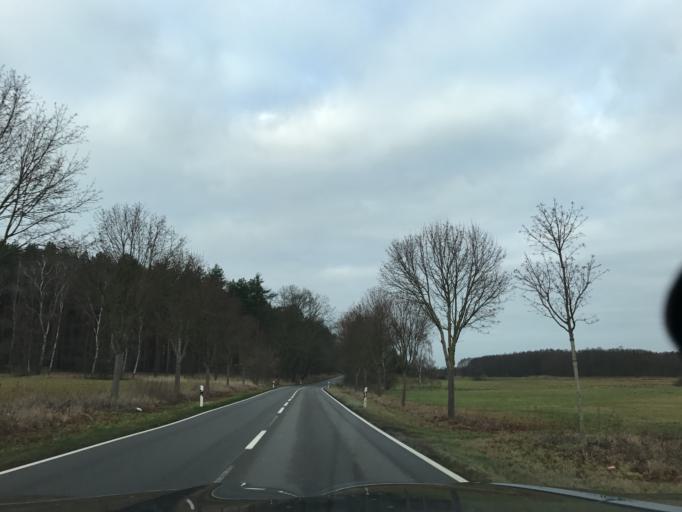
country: DE
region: Brandenburg
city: Brandenburg an der Havel
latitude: 52.3553
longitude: 12.6083
